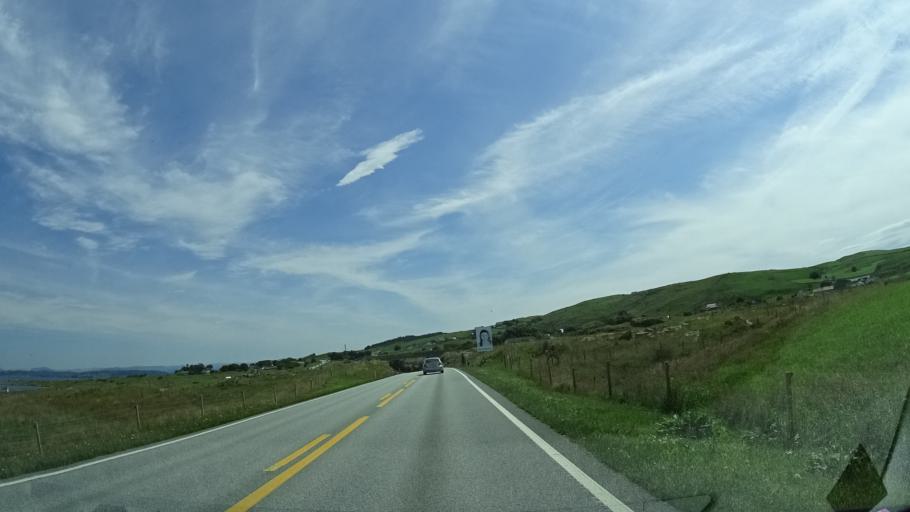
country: NO
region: Rogaland
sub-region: Rennesoy
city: Vikevag
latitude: 59.1280
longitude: 5.6207
